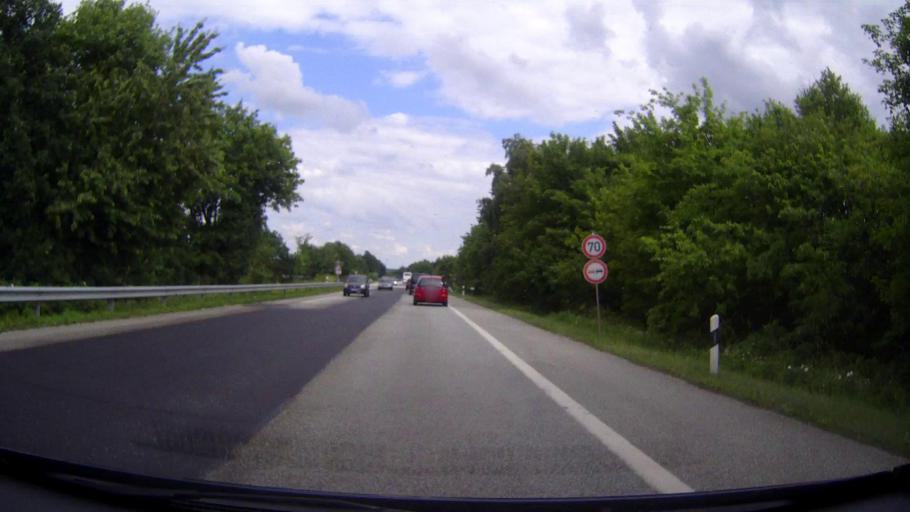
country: DE
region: Schleswig-Holstein
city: Klein Gladebrugge
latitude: 53.9230
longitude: 10.3320
